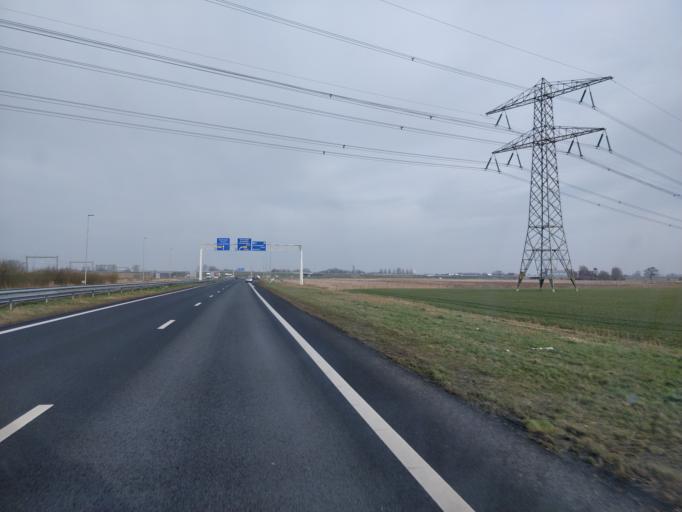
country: NL
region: Friesland
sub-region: Gemeente Leeuwarden
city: Wirdum
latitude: 53.1504
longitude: 5.7933
